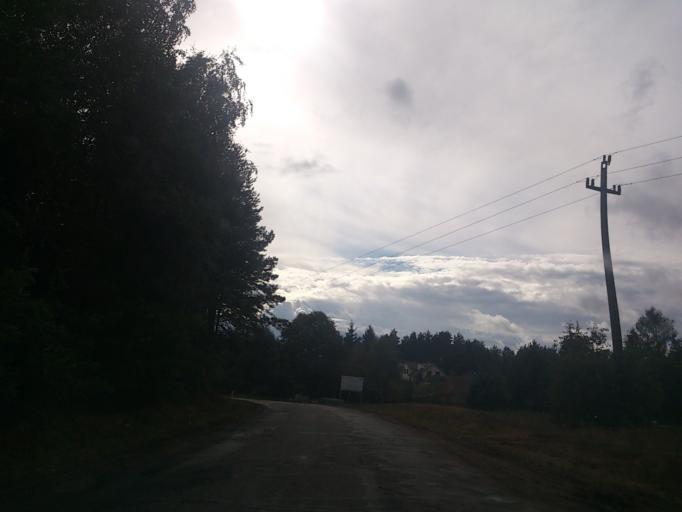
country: PL
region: Greater Poland Voivodeship
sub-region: Powiat poznanski
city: Kobylnica
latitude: 52.5186
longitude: 17.1417
